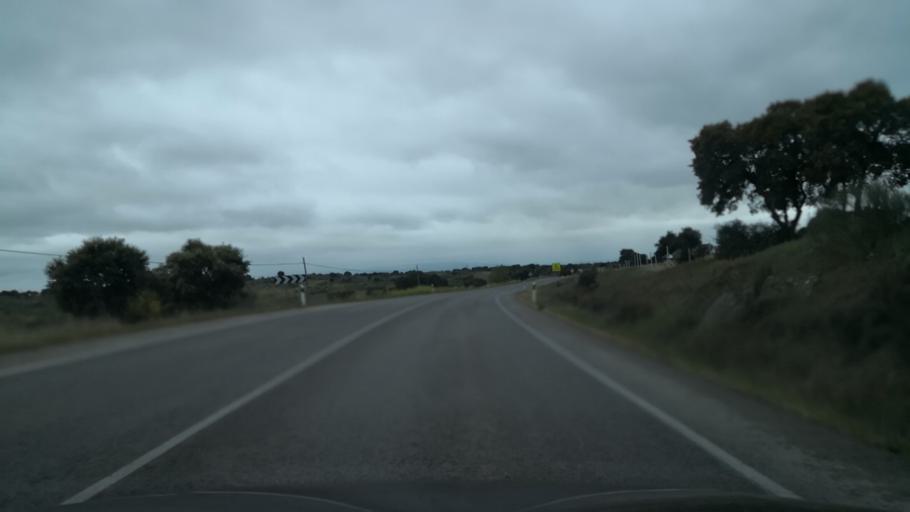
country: ES
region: Extremadura
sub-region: Provincia de Caceres
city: Caceres
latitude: 39.4107
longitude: -6.4152
